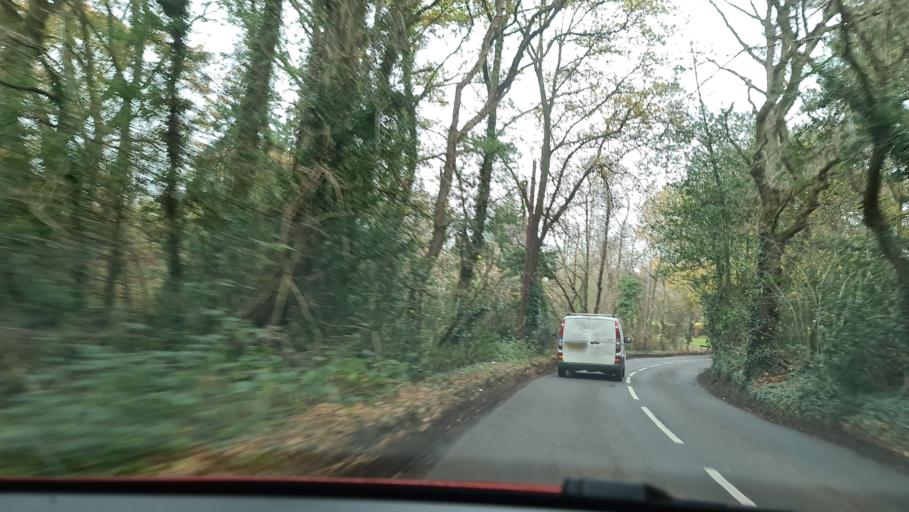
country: GB
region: England
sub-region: Buckinghamshire
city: Seer Green
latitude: 51.6173
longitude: -0.5917
